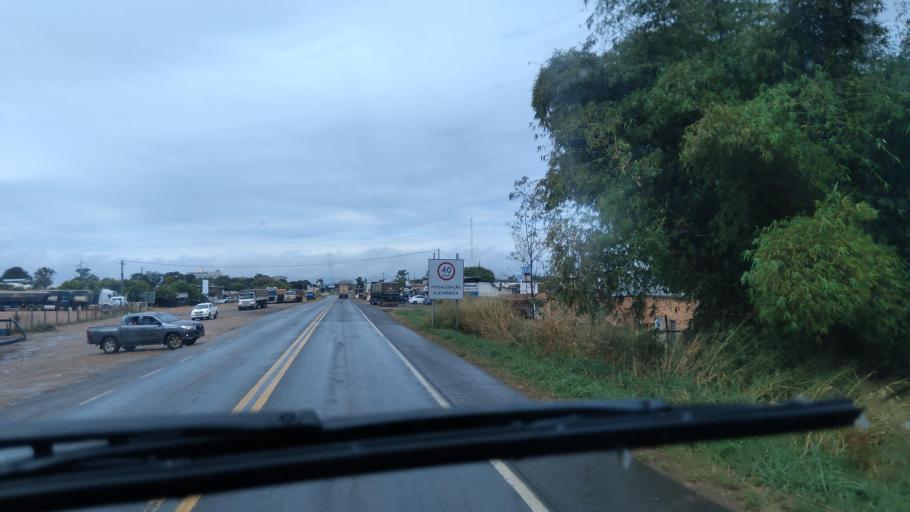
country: BR
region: Goias
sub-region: Mineiros
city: Mineiros
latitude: -17.5519
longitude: -52.5282
